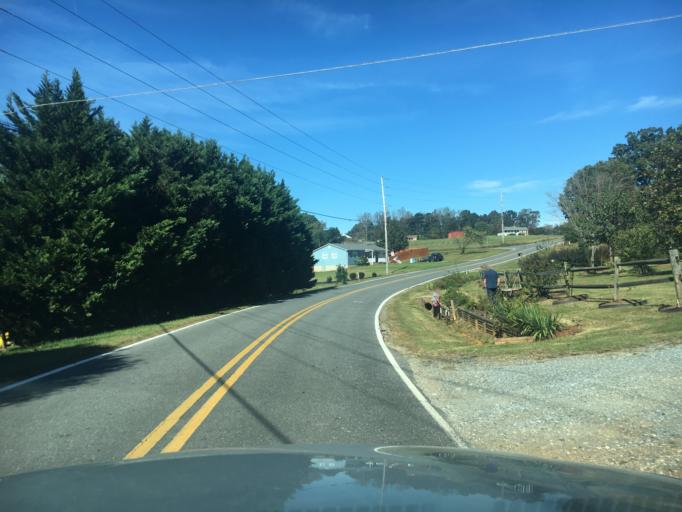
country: US
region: North Carolina
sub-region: Burke County
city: Salem
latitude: 35.6937
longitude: -81.7362
